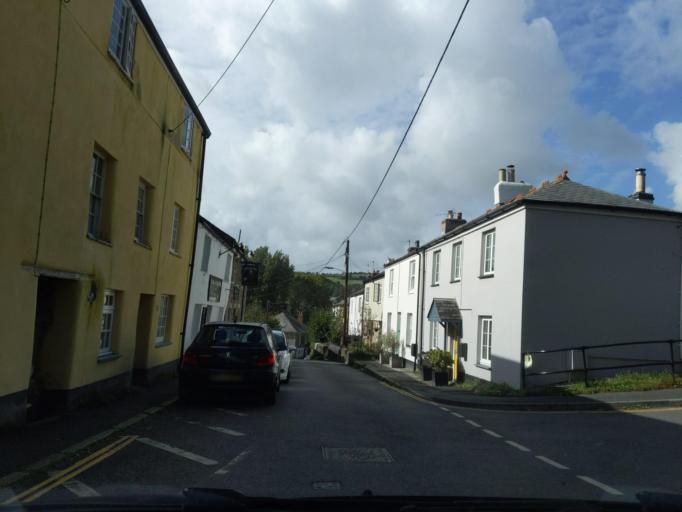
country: GB
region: England
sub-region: Cornwall
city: Lostwithiel
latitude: 50.4069
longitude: -4.6626
